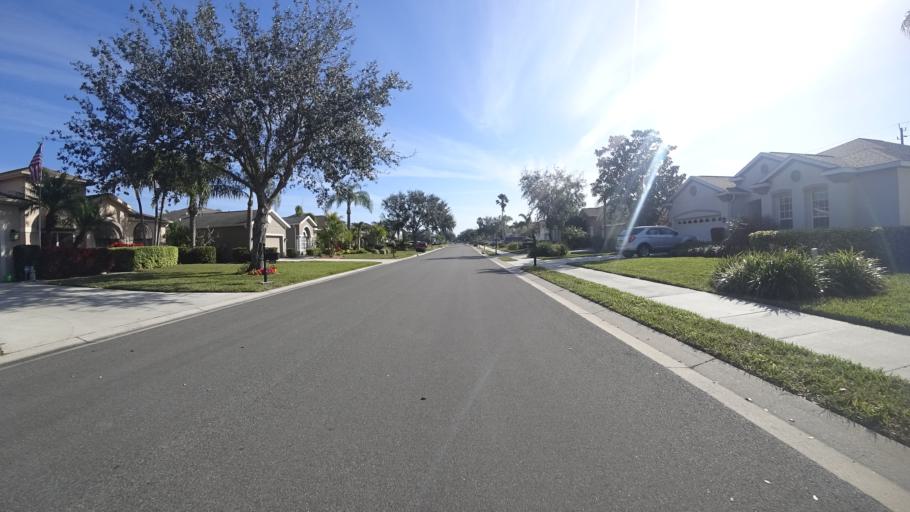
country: US
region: Florida
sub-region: Manatee County
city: Bayshore Gardens
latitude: 27.4484
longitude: -82.6179
